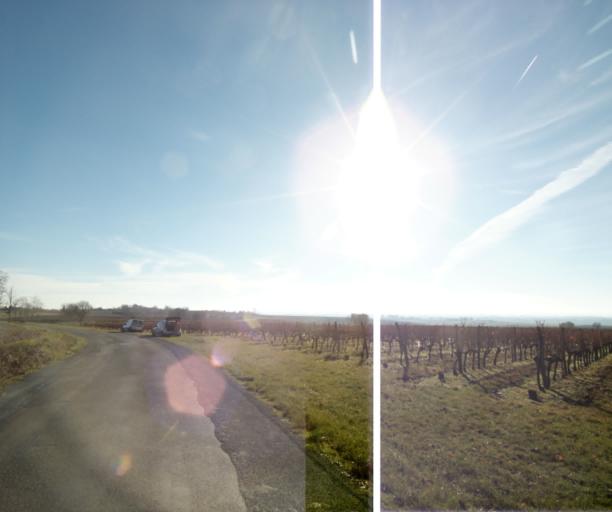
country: FR
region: Poitou-Charentes
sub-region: Departement de la Charente-Maritime
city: Chaniers
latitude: 45.7387
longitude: -0.5672
